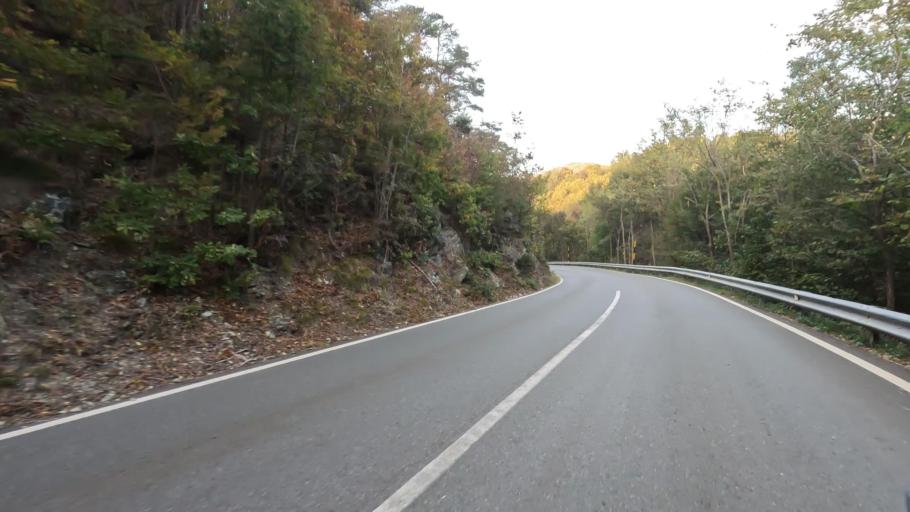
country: IT
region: Liguria
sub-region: Provincia di Savona
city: Sassello
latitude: 44.5069
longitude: 8.4823
